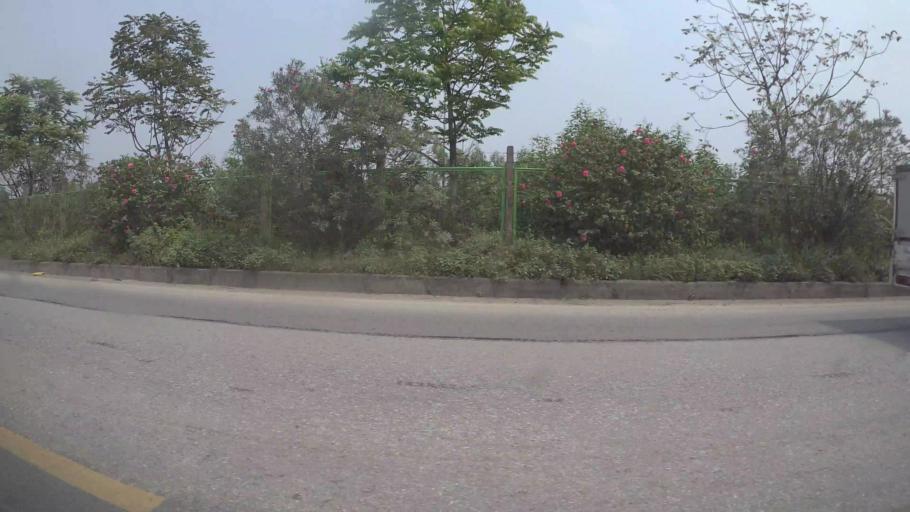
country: VN
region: Ha Noi
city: Quoc Oai
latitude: 21.0014
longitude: 105.6232
